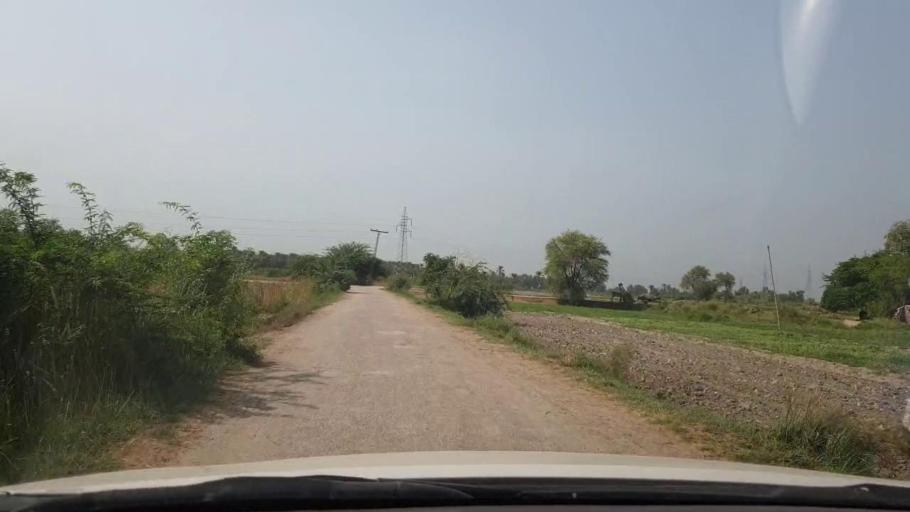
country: PK
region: Sindh
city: Shikarpur
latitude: 27.9771
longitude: 68.6737
